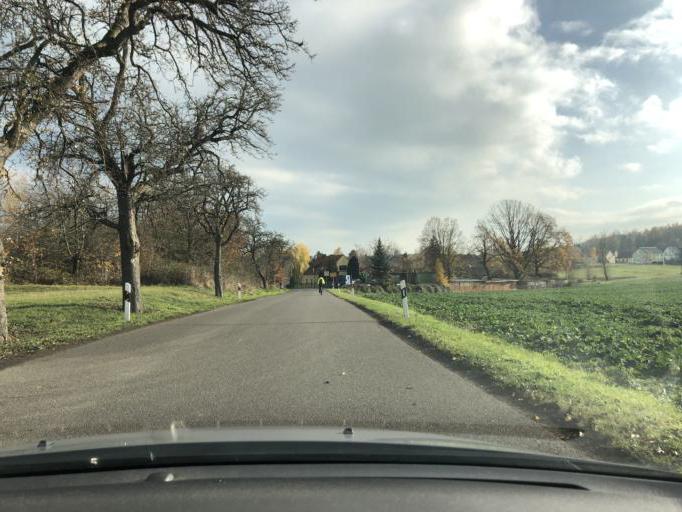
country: DE
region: Saxony
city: Nerchau
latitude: 51.2550
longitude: 12.7613
